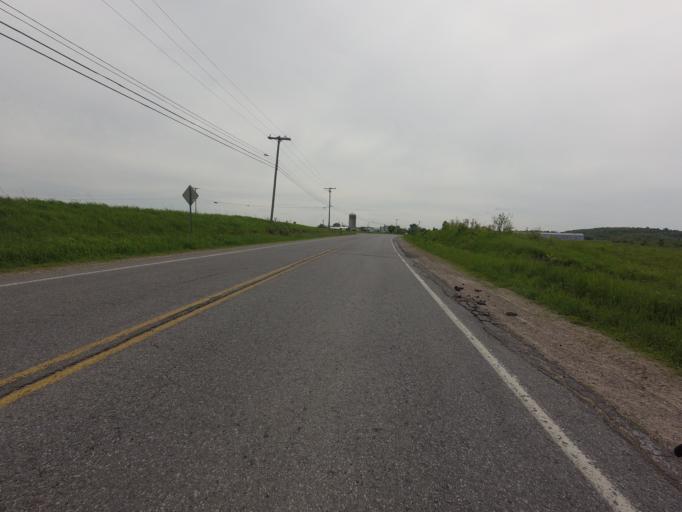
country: US
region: New York
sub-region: St. Lawrence County
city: Gouverneur
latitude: 44.3510
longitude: -75.2169
